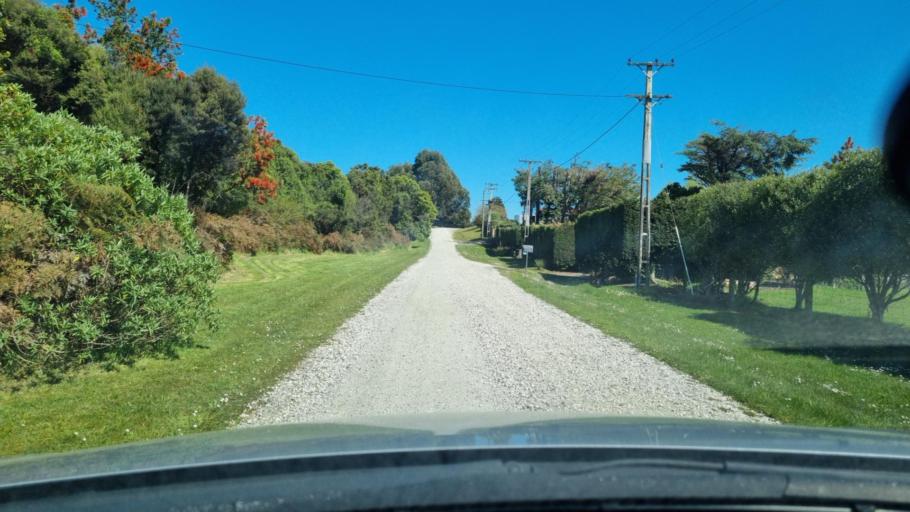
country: NZ
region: Southland
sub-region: Invercargill City
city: Invercargill
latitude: -46.4209
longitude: 168.2884
